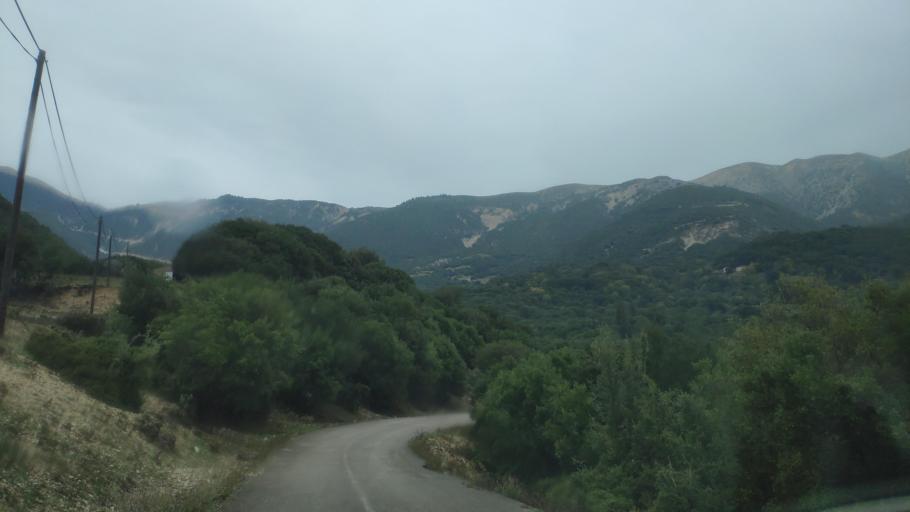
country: GR
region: Epirus
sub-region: Nomos Thesprotias
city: Paramythia
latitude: 39.4199
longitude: 20.6176
